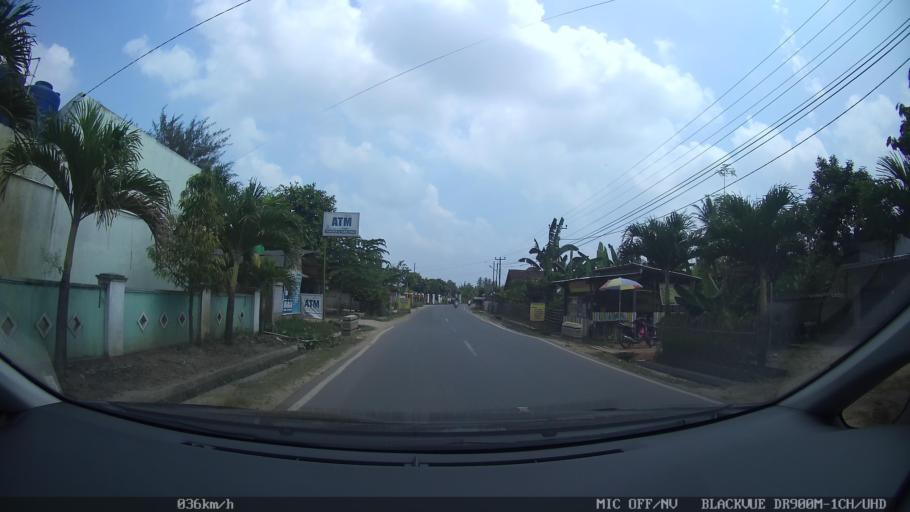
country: ID
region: Lampung
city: Pringsewu
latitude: -5.3821
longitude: 104.9688
